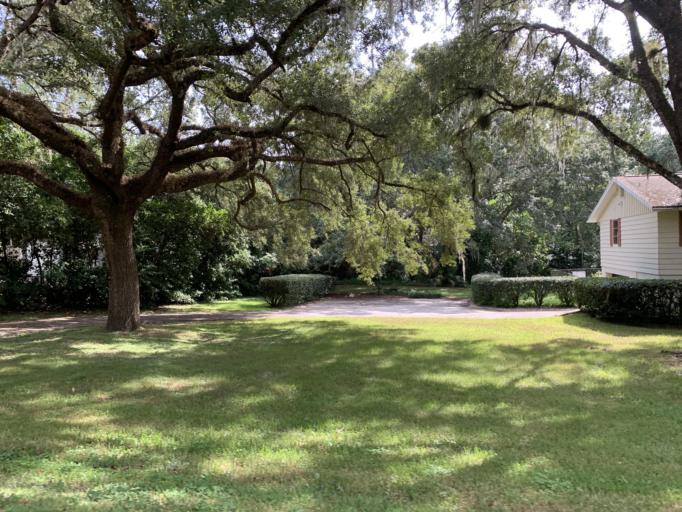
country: US
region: Florida
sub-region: Marion County
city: Ocala
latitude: 29.1794
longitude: -82.1129
